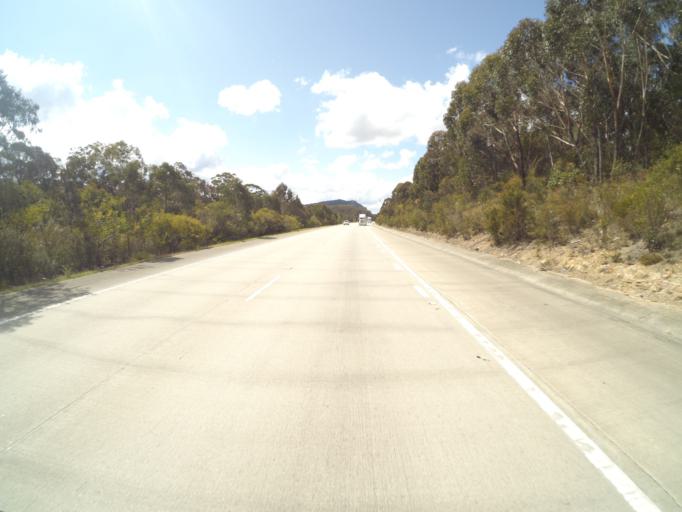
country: AU
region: New South Wales
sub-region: Wingecarribee
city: Mittagong
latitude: -34.4347
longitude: 150.4284
